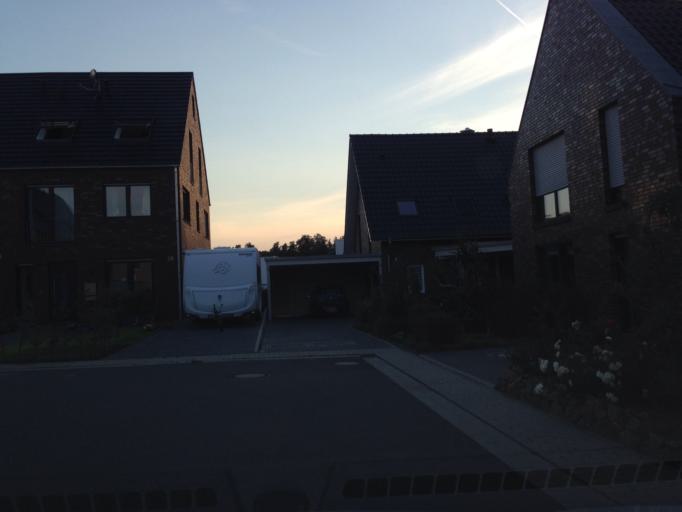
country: DE
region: North Rhine-Westphalia
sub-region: Regierungsbezirk Munster
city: Muenster
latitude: 51.9015
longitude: 7.6205
